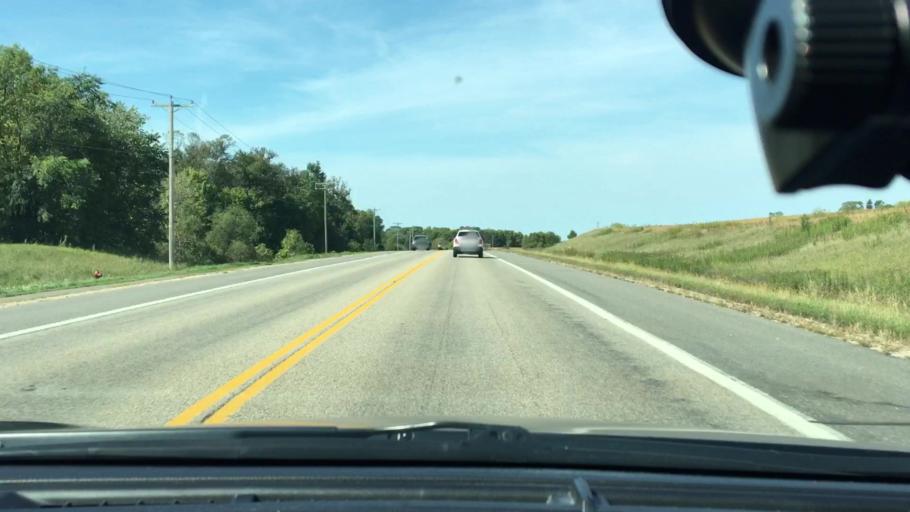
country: US
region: Minnesota
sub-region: Wright County
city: Hanover
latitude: 45.1633
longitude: -93.6711
